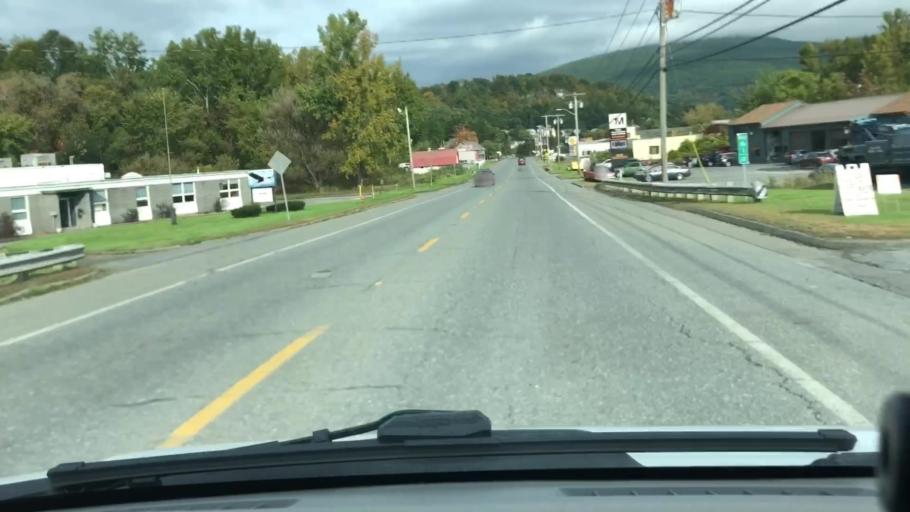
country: US
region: Massachusetts
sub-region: Berkshire County
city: North Adams
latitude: 42.6861
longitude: -73.1088
